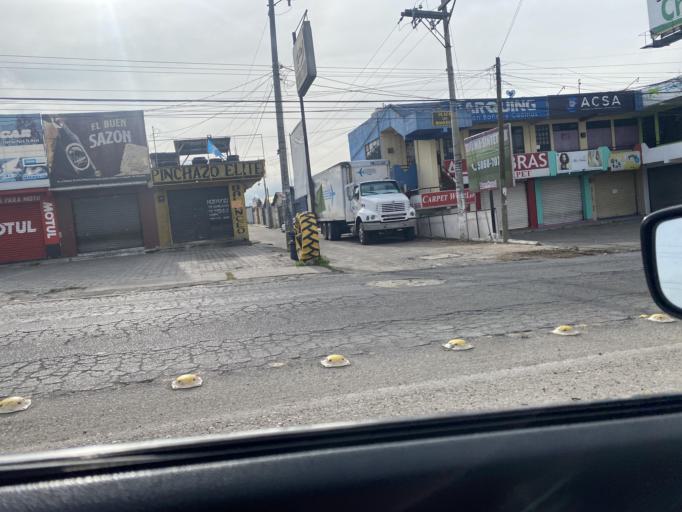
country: GT
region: Quetzaltenango
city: Quetzaltenango
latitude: 14.8565
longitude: -91.5216
